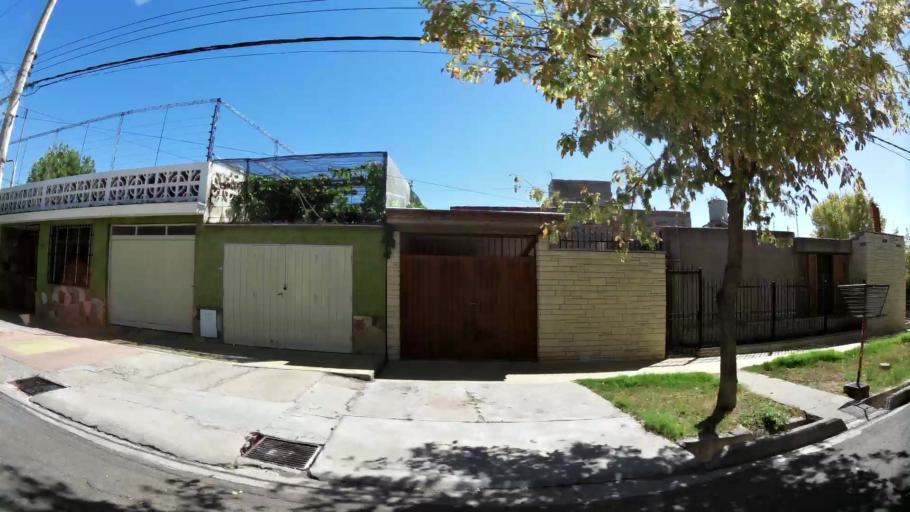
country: AR
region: Mendoza
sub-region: Departamento de Godoy Cruz
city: Godoy Cruz
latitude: -32.9396
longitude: -68.8571
